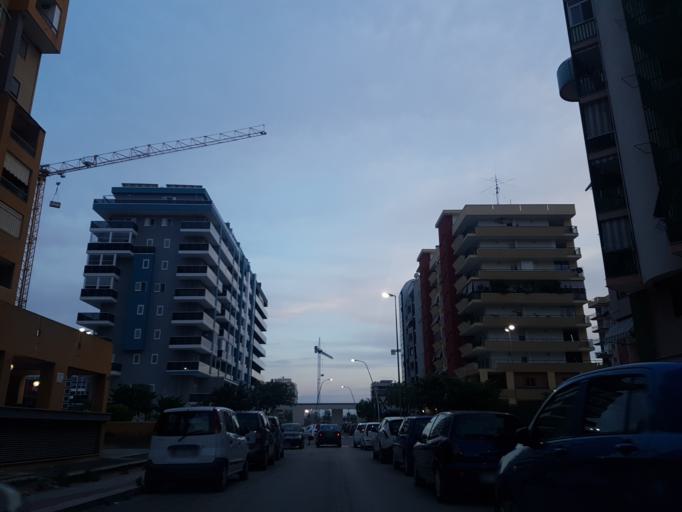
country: IT
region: Apulia
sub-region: Provincia di Barletta - Andria - Trani
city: Barletta
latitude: 41.3066
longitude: 16.2748
